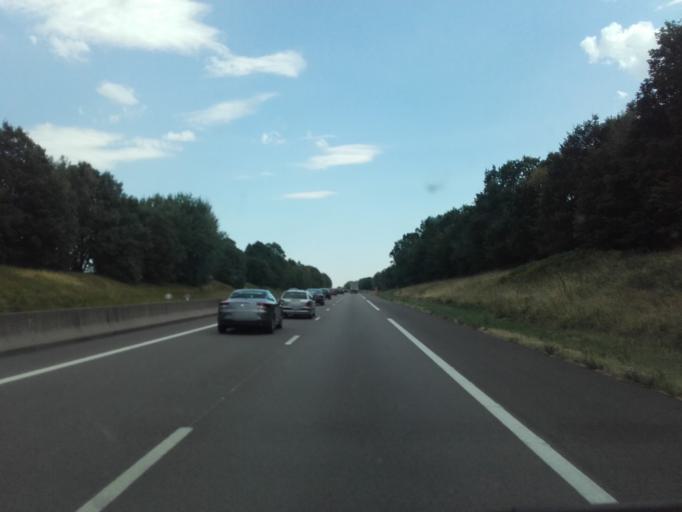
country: FR
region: Bourgogne
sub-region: Departement de la Cote-d'Or
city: Semur-en-Auxois
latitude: 47.4595
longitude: 4.2559
